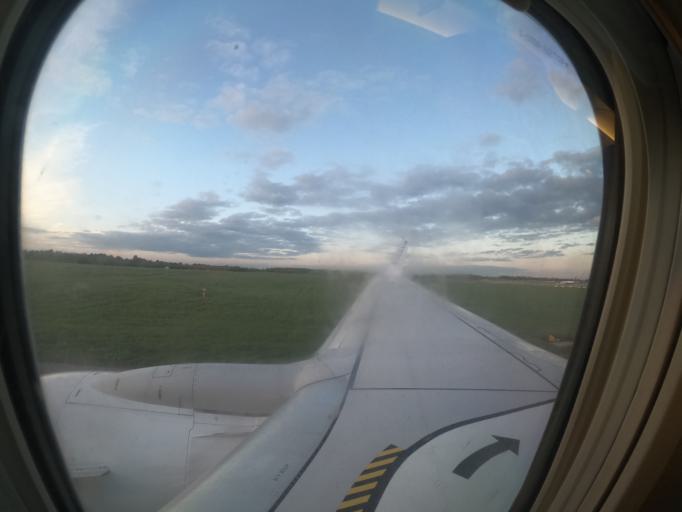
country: GB
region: England
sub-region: Essex
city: Takeley
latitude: 51.8949
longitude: 0.2522
